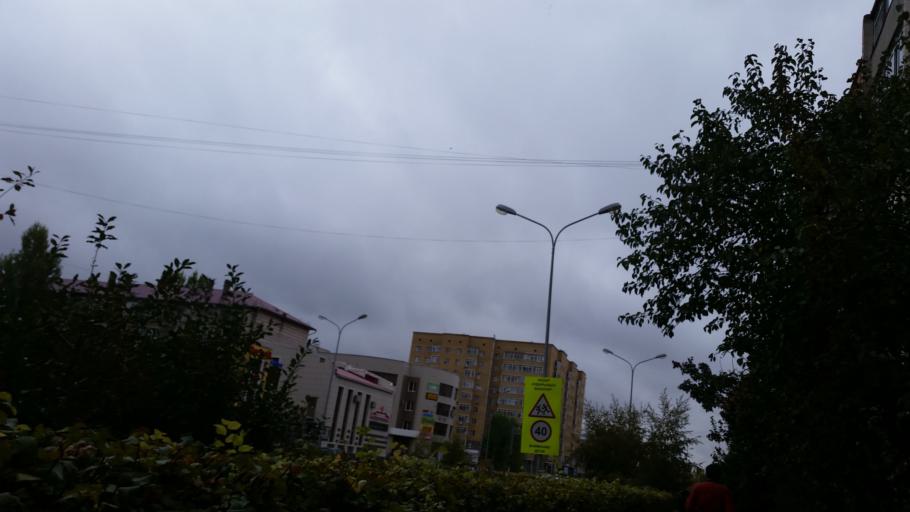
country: KZ
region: Astana Qalasy
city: Astana
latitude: 51.1541
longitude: 71.5021
